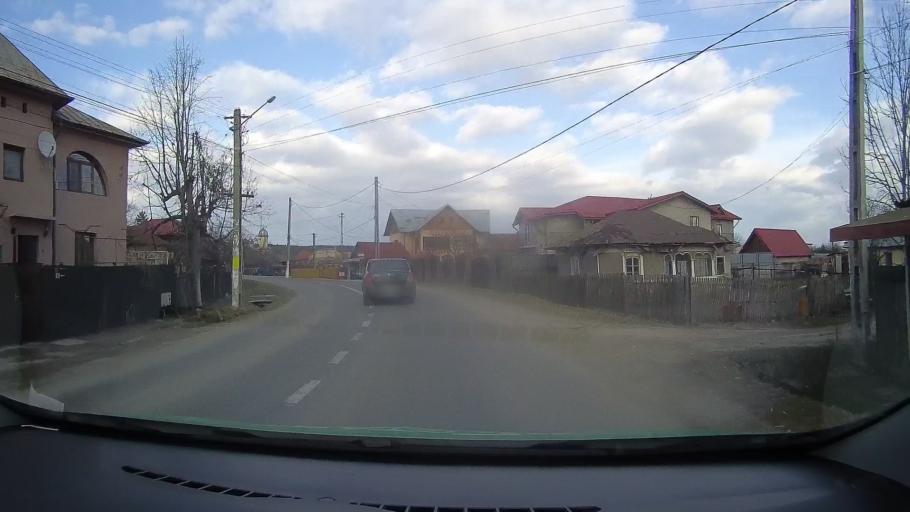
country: RO
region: Dambovita
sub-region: Comuna Gura Ocnitei
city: Gura Ocnitei
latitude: 44.9369
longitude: 25.5631
